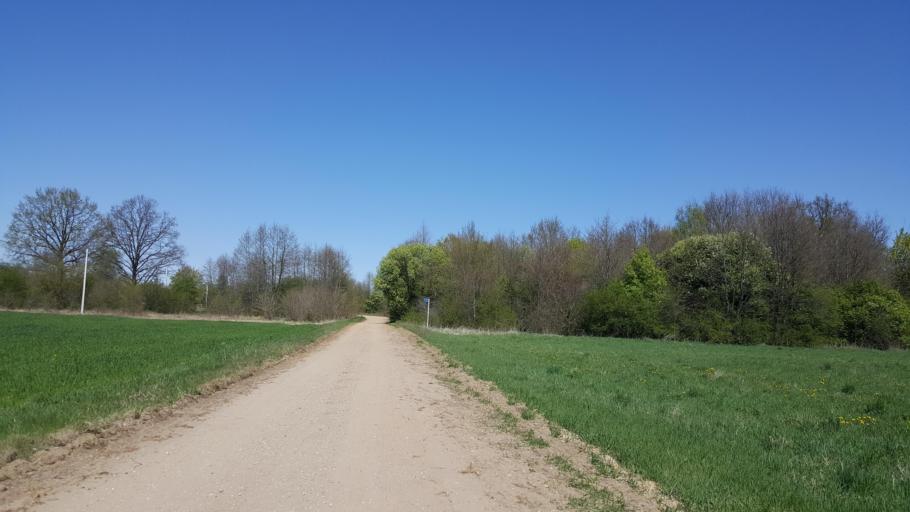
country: BY
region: Brest
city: Kamyanyets
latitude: 52.3343
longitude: 23.7492
